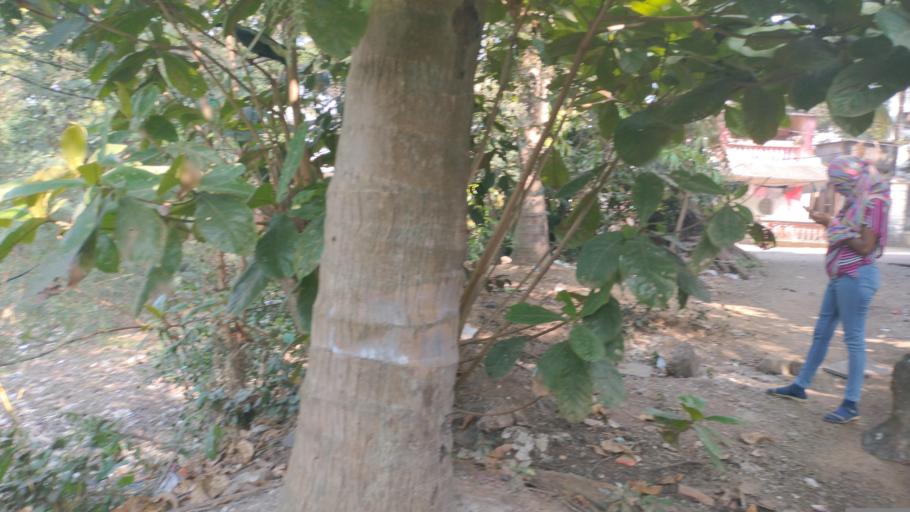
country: IN
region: Maharashtra
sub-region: Thane
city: Virar
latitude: 19.5155
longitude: 72.8526
